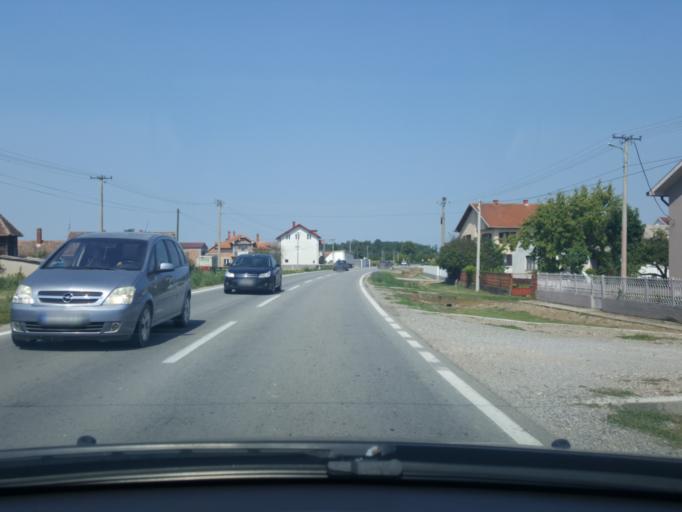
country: RS
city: Dublje
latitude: 44.7520
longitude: 19.5286
